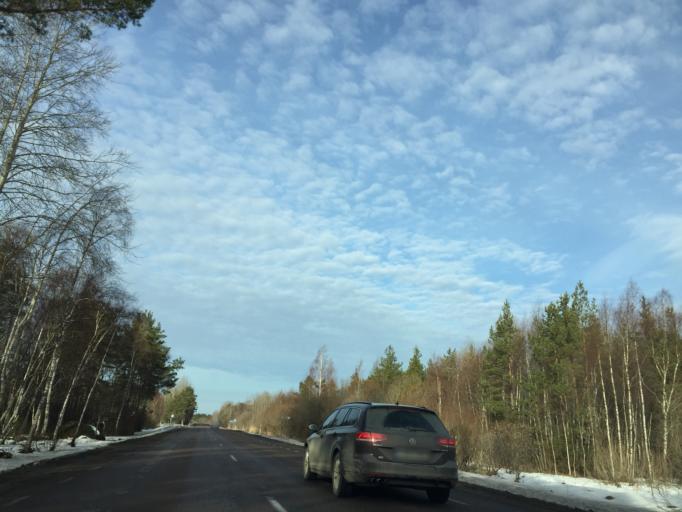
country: EE
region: Saare
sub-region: Kuressaare linn
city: Kuressaare
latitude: 58.2795
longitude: 22.4336
